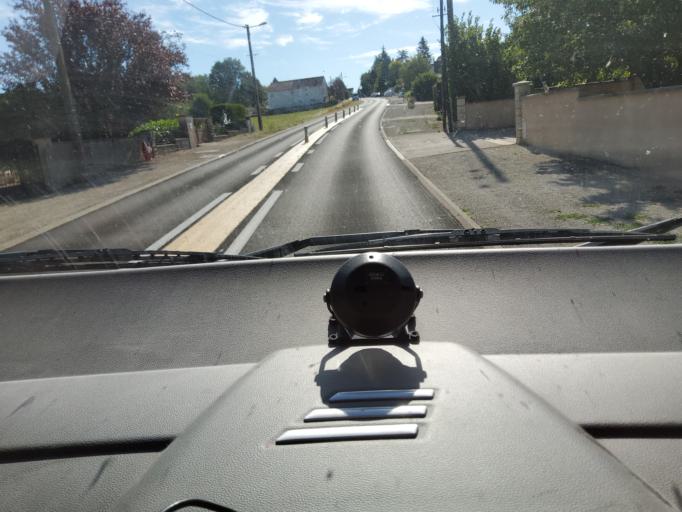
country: FR
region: Franche-Comte
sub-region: Departement du Jura
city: Champvans
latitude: 47.1058
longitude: 5.4445
